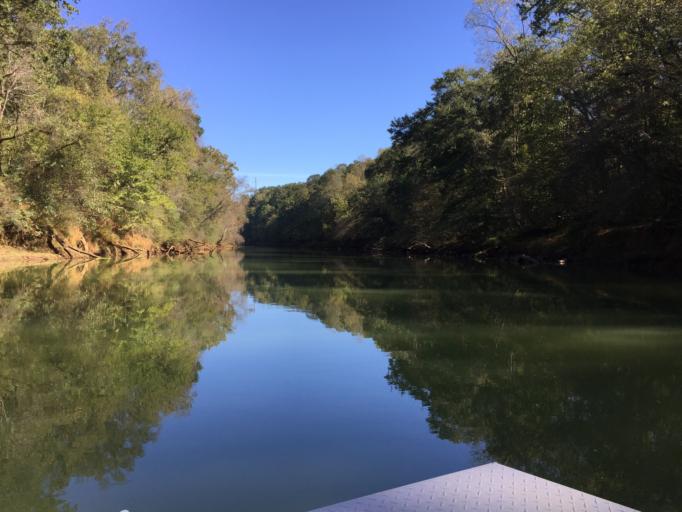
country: US
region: Georgia
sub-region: Gwinnett County
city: Suwanee
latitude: 34.0470
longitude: -84.1013
